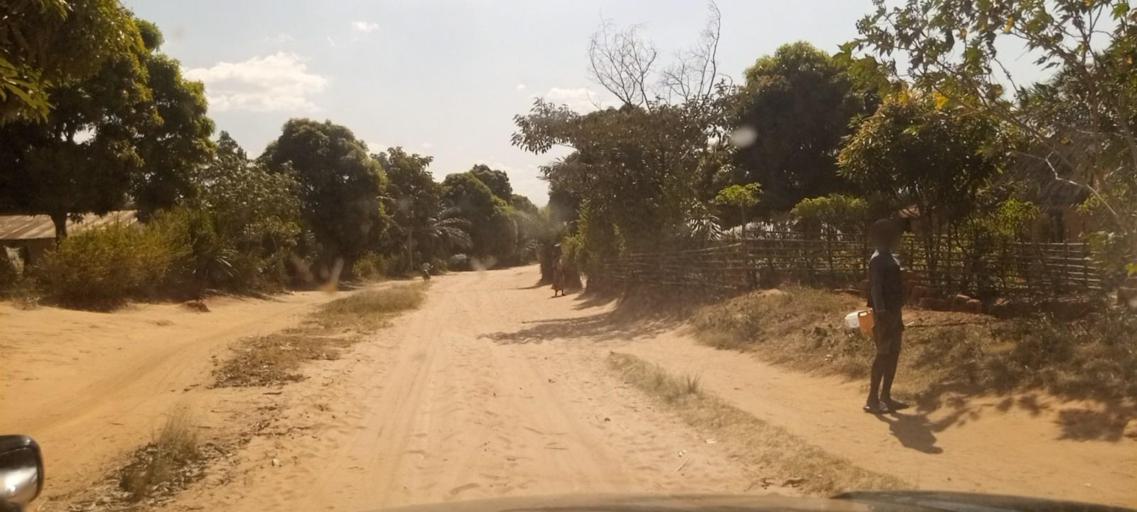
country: CD
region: Kasai-Oriental
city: Kabinda
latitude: -6.1318
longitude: 24.5085
